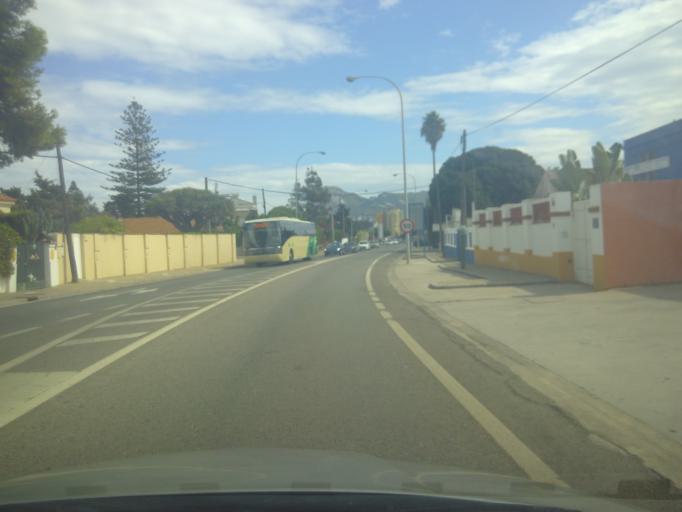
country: ES
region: Andalusia
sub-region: Provincia de Cadiz
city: La Linea de la Concepcion
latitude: 36.1758
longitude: -5.3746
